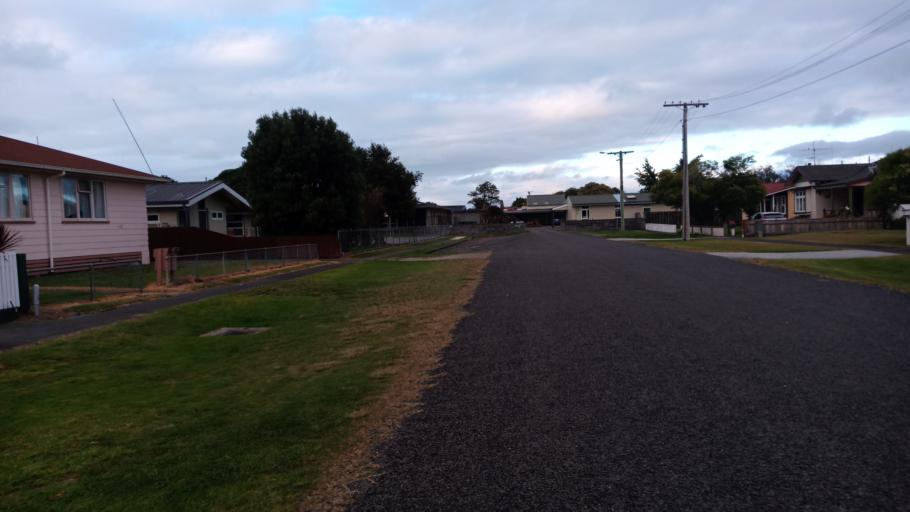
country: NZ
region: Gisborne
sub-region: Gisborne District
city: Gisborne
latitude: -38.6568
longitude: 178.0072
